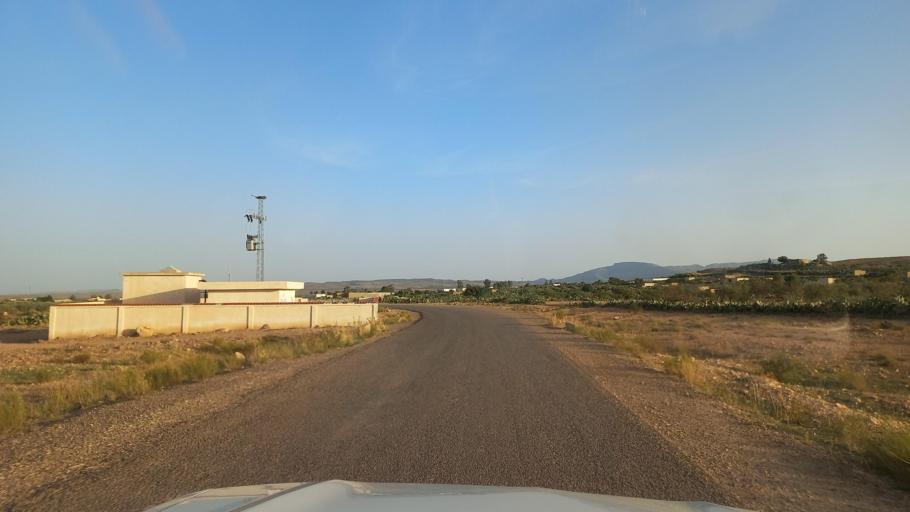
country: TN
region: Al Qasrayn
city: Kasserine
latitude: 35.2639
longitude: 8.9346
